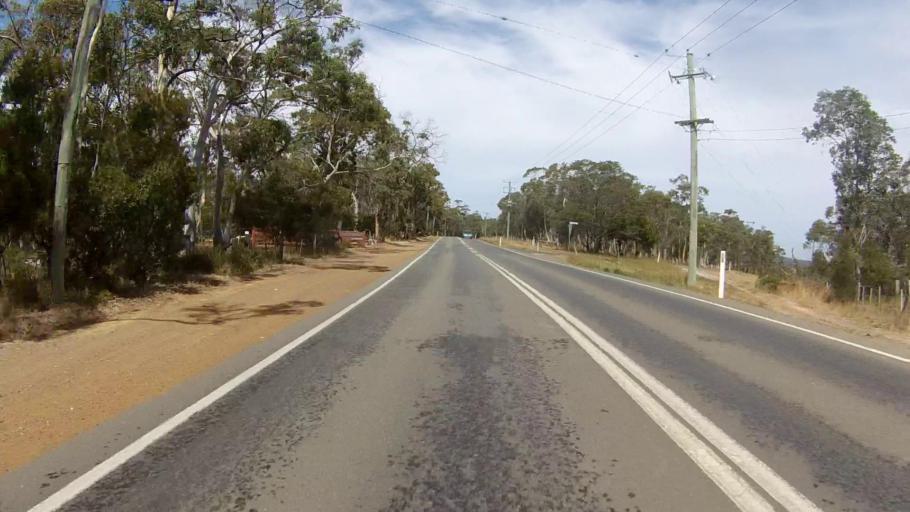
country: AU
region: Tasmania
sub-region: Clarence
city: Sandford
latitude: -42.9719
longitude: 147.5036
